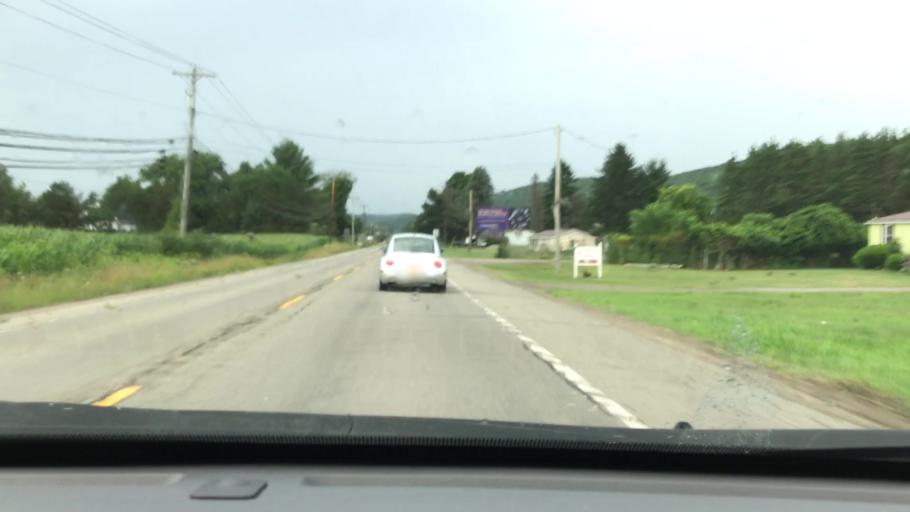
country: US
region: New York
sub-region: Cattaraugus County
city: Salamanca
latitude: 42.2024
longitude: -78.6469
